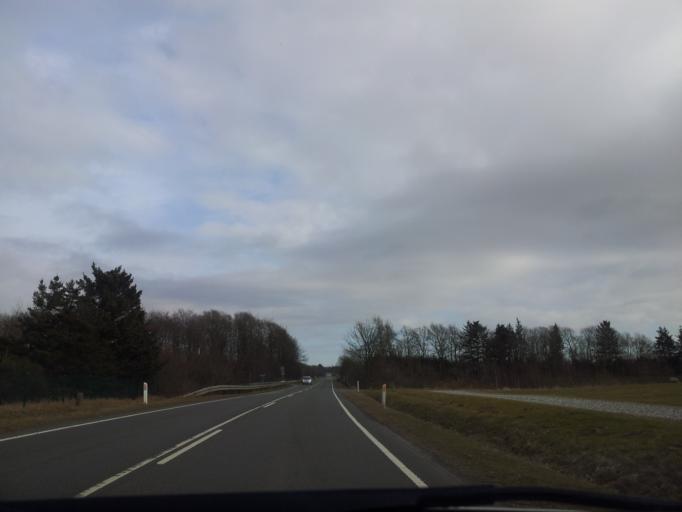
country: DK
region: South Denmark
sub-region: Vejen Kommune
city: Brorup
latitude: 55.4453
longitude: 9.0468
